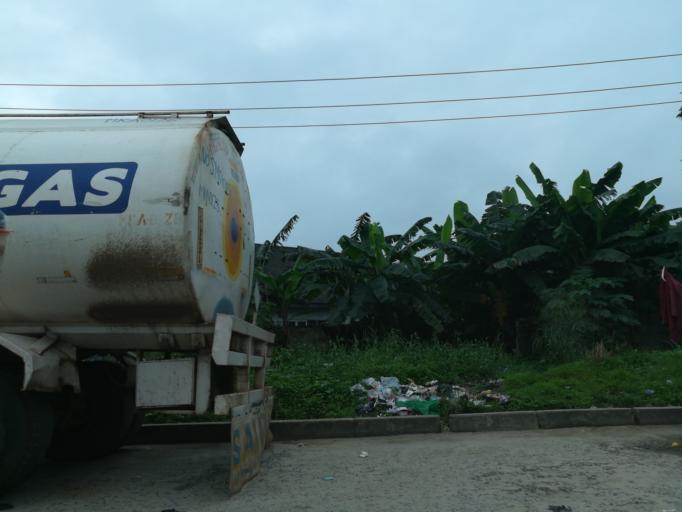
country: NG
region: Rivers
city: Port Harcourt
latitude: 4.7620
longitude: 7.0116
